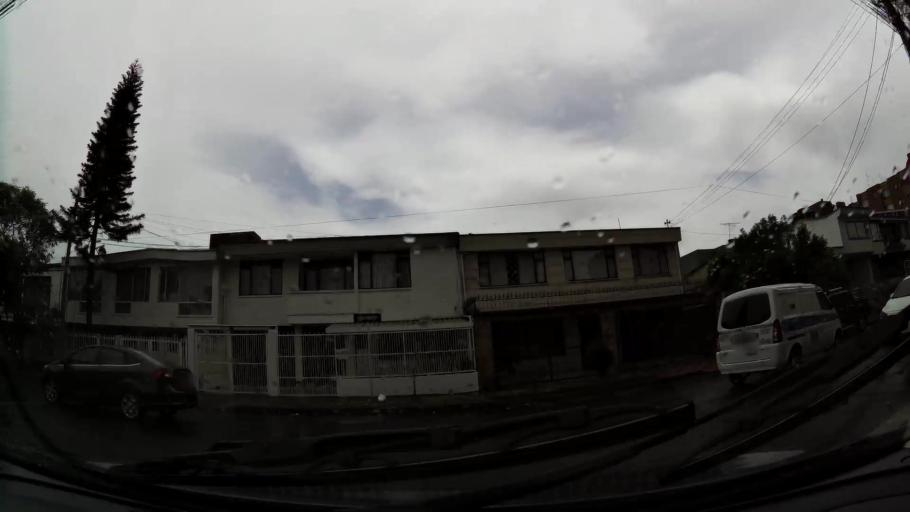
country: CO
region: Bogota D.C.
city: Bogota
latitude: 4.6522
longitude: -74.1005
